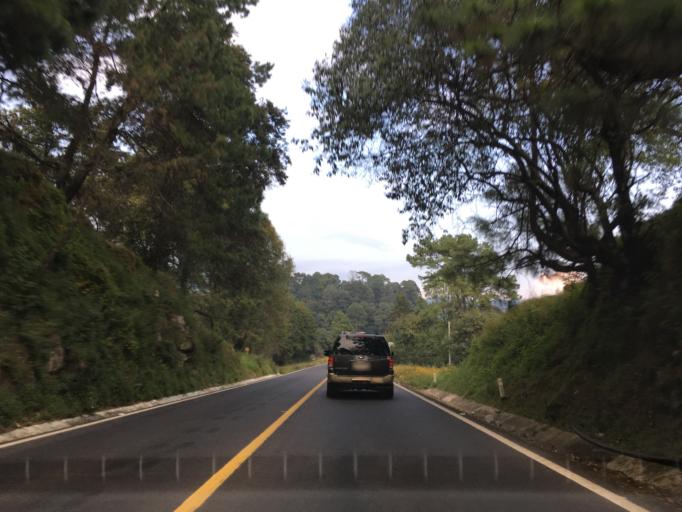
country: MX
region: Michoacan
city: Tingambato
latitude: 19.4922
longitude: -101.8765
